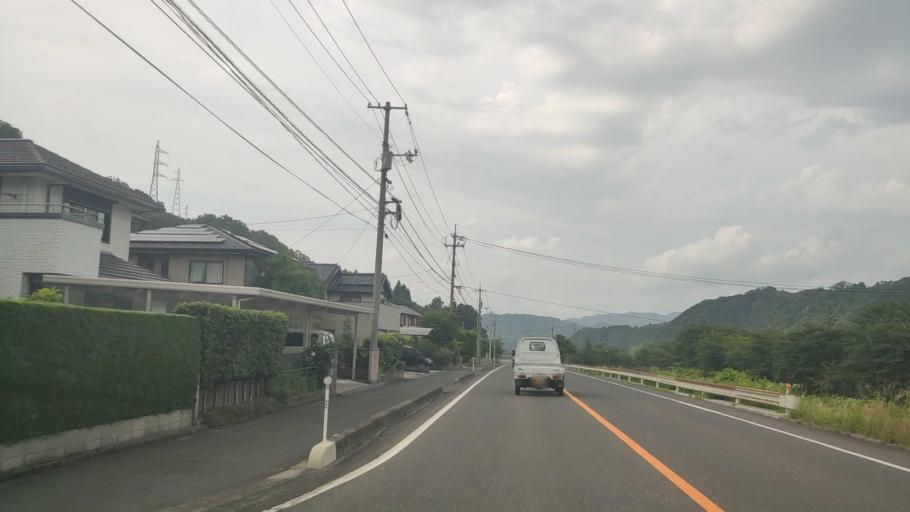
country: JP
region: Tottori
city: Kurayoshi
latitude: 35.3870
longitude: 133.8565
